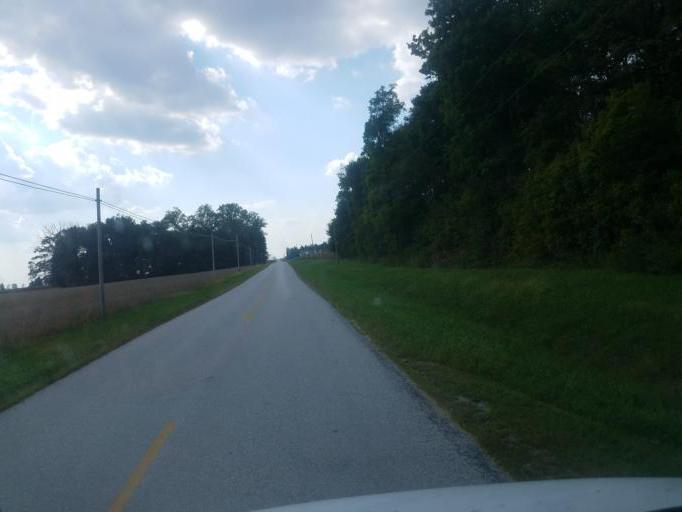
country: US
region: Ohio
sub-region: Hancock County
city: Arlington
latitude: 40.7906
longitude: -83.6864
